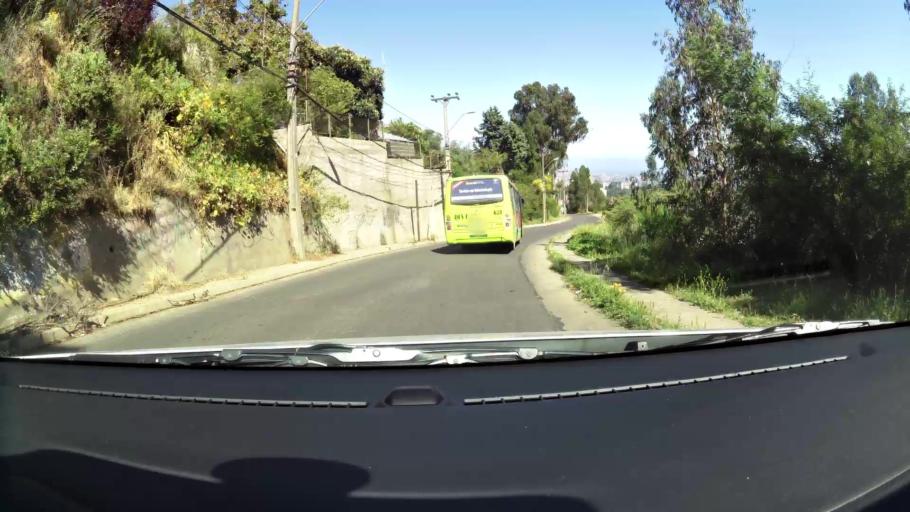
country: CL
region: Valparaiso
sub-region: Provincia de Valparaiso
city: Vina del Mar
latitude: -33.0624
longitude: -71.5756
